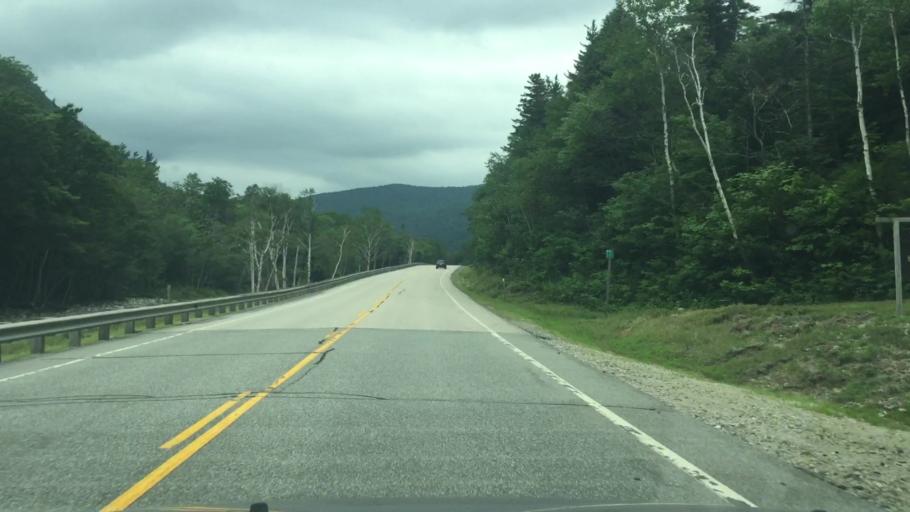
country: US
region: New Hampshire
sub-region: Grafton County
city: Deerfield
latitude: 44.1900
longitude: -71.4037
